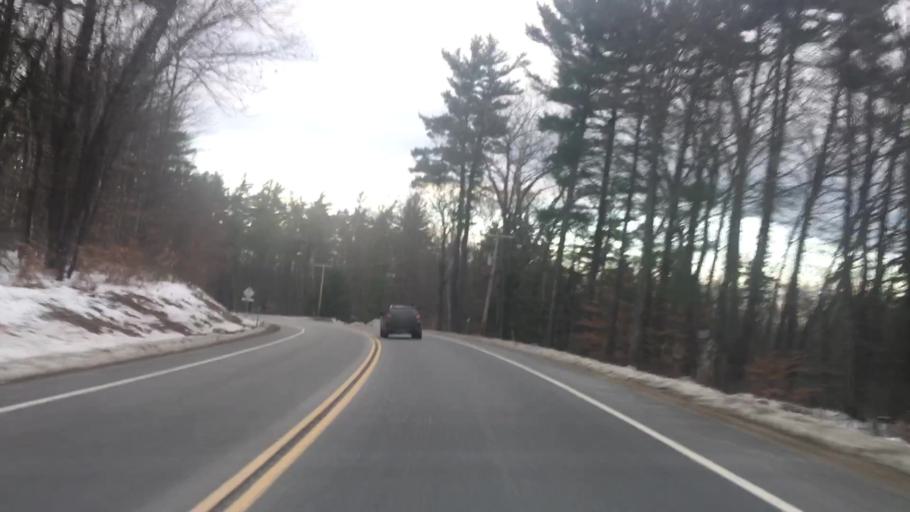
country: US
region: New Hampshire
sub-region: Hillsborough County
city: Antrim
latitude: 43.0839
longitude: -71.9650
